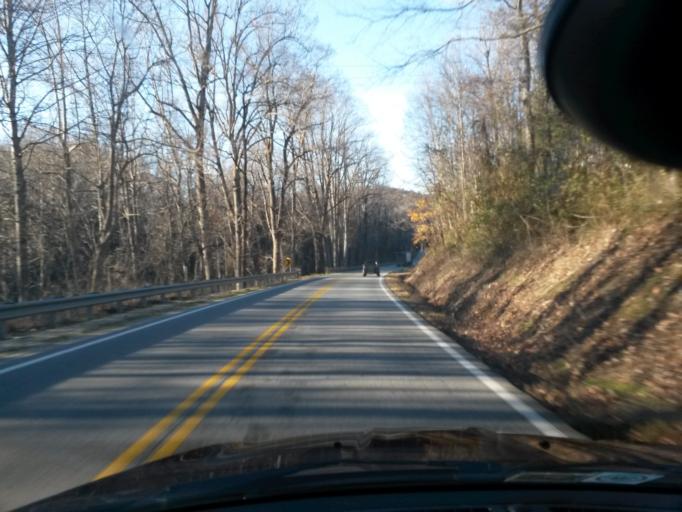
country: US
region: Virginia
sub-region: Amherst County
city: Amherst
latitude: 37.6253
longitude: -79.1158
